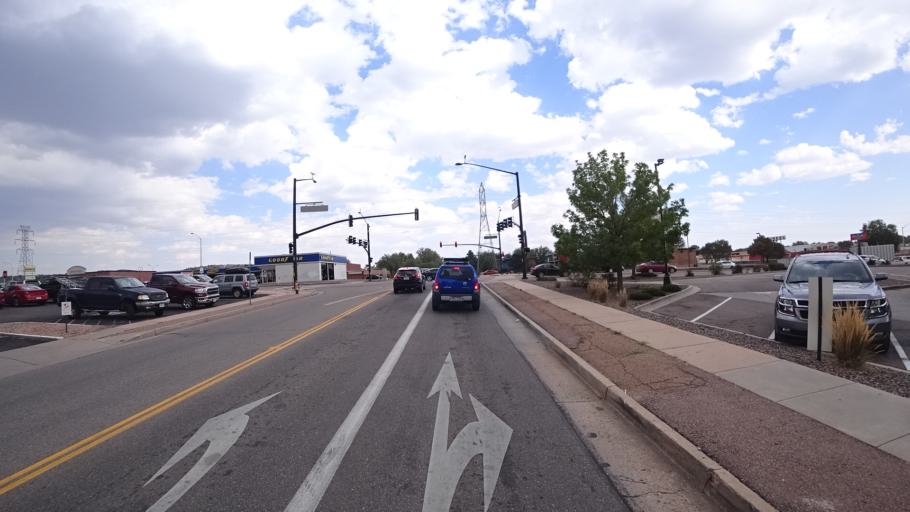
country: US
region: Colorado
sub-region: El Paso County
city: Cimarron Hills
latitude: 38.8512
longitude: -104.7579
